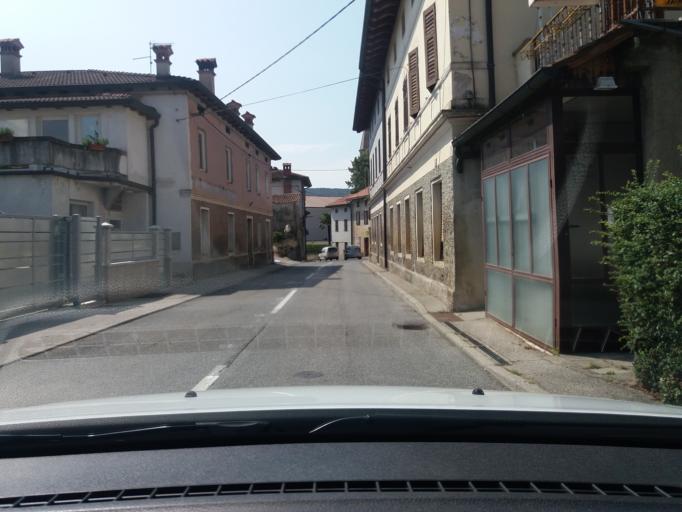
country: SI
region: Miren-Kostanjevica
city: Miren
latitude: 45.8962
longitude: 13.6082
